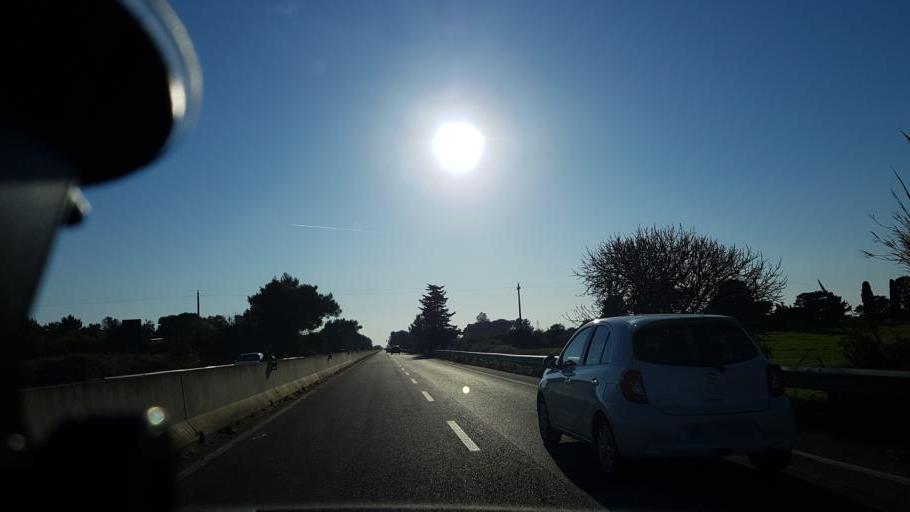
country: IT
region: Apulia
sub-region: Provincia di Lecce
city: Struda
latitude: 40.3797
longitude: 18.2670
